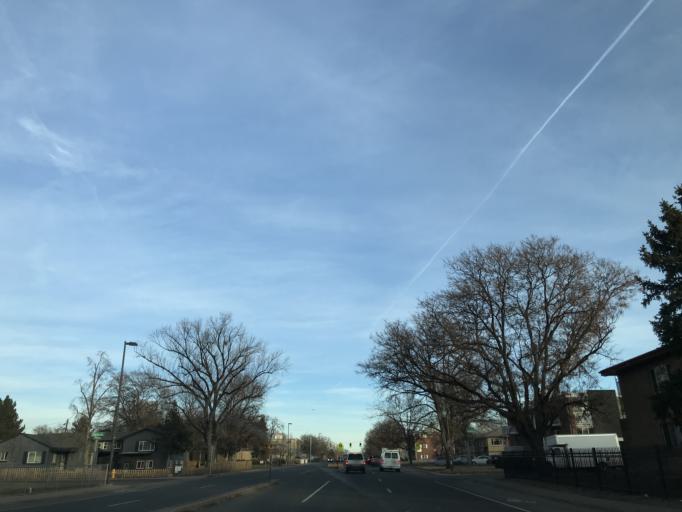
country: US
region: Colorado
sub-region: Adams County
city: Aurora
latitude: 39.7474
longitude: -104.8735
